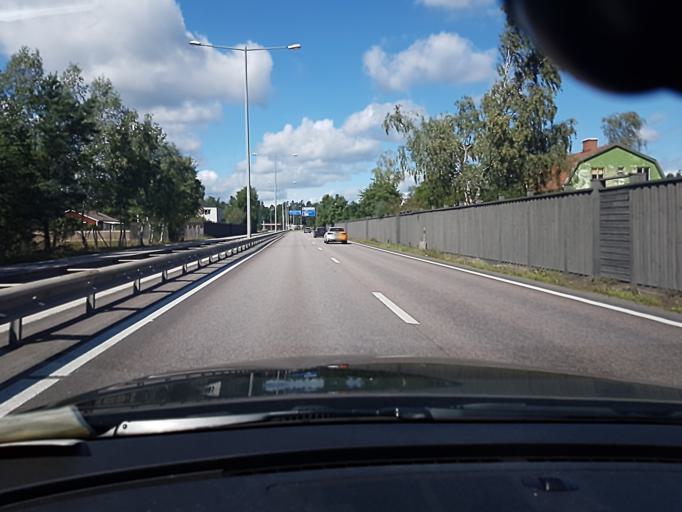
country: SE
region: Kalmar
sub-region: Nybro Kommun
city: Nybro
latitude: 56.7342
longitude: 15.9380
